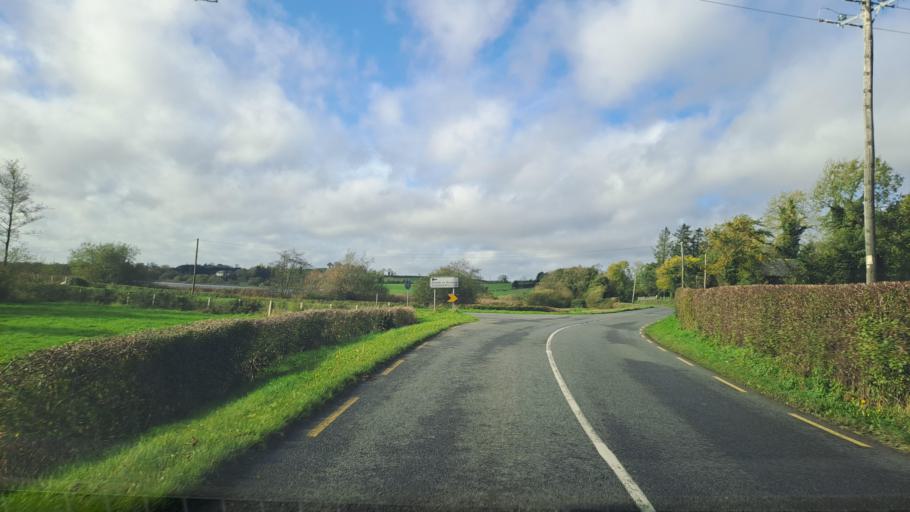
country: IE
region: Ulster
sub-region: An Cabhan
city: Cootehill
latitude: 54.1087
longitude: -6.9616
